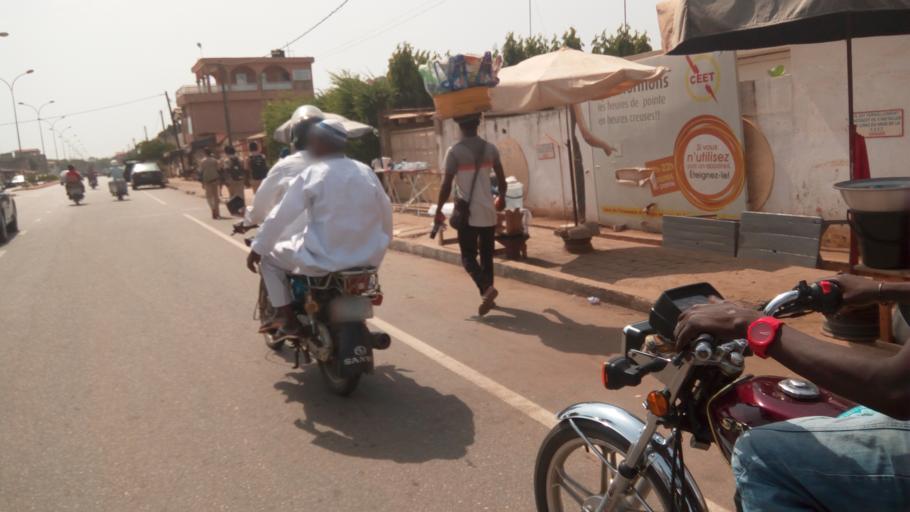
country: TG
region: Maritime
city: Lome
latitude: 6.1703
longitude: 1.2318
